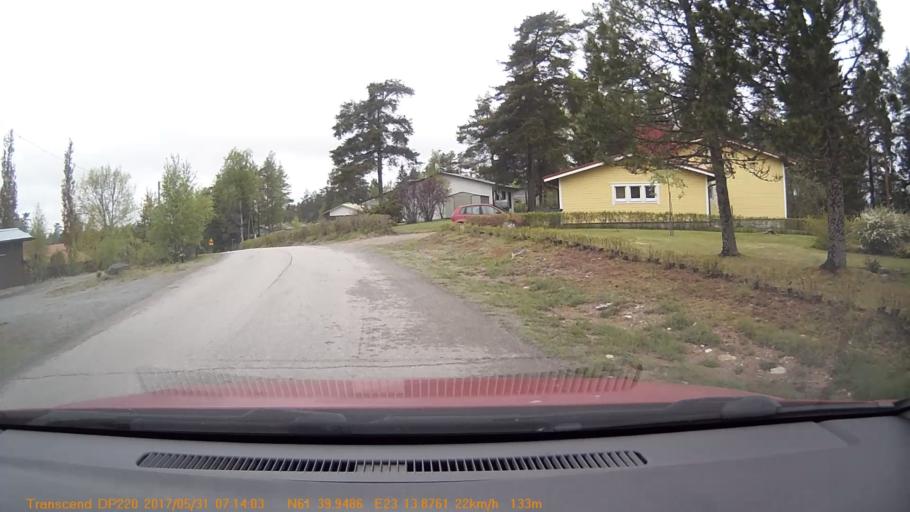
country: FI
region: Pirkanmaa
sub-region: Tampere
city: Haemeenkyroe
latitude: 61.6657
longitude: 23.2309
